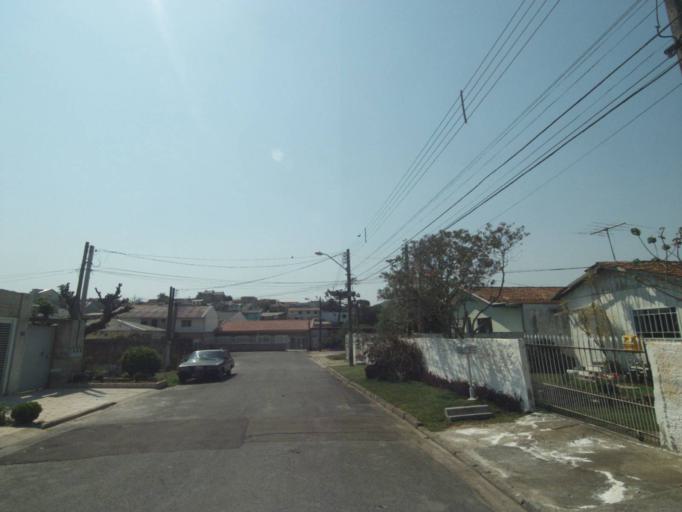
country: BR
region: Parana
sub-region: Sao Jose Dos Pinhais
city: Sao Jose dos Pinhais
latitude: -25.5109
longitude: -49.2706
